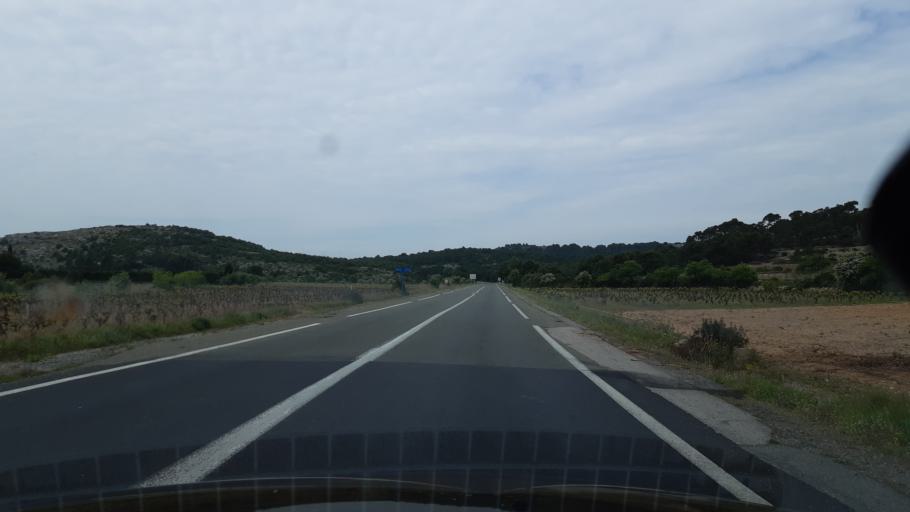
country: FR
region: Languedoc-Roussillon
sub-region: Departement de l'Aude
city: Gruissan
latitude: 43.1173
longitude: 3.0879
